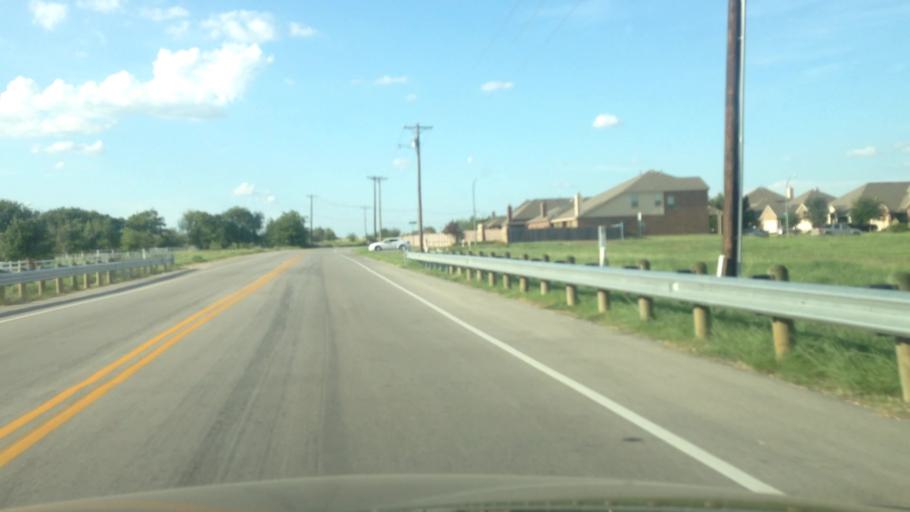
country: US
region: Texas
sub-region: Tarrant County
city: Haslet
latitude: 32.9826
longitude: -97.3980
